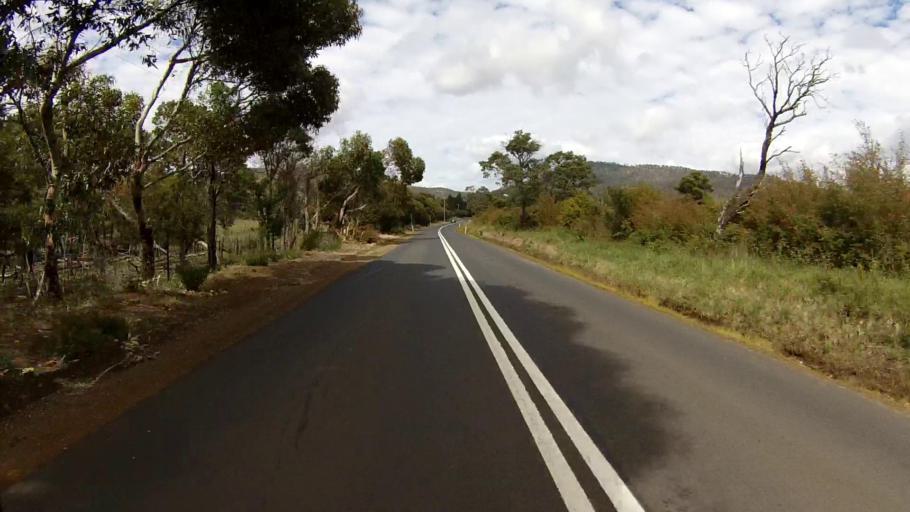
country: AU
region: Tasmania
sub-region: Clarence
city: Cambridge
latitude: -42.7588
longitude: 147.4027
